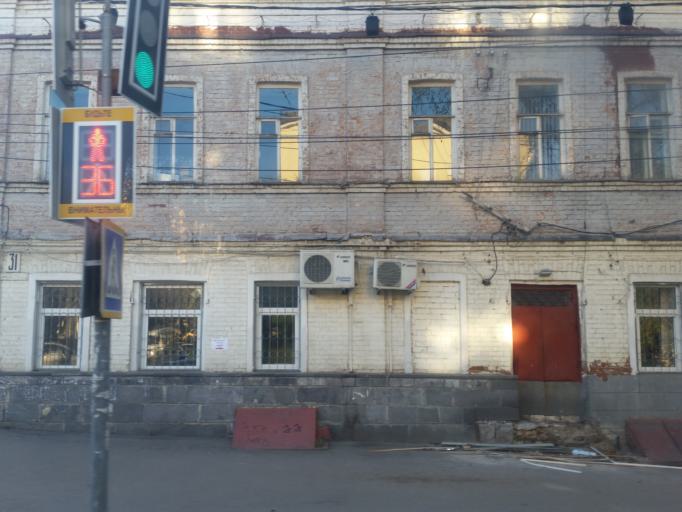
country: RU
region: Ulyanovsk
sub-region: Ulyanovskiy Rayon
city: Ulyanovsk
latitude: 54.3209
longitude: 48.3909
